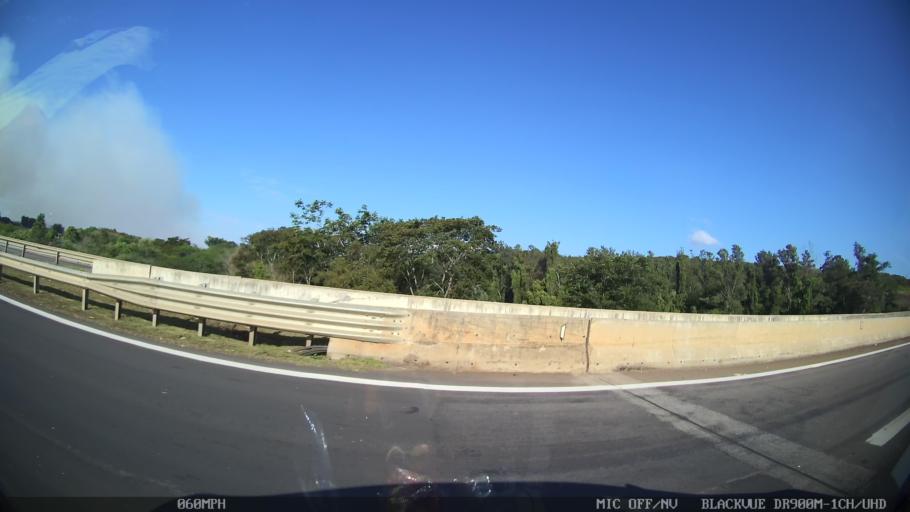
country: BR
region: Sao Paulo
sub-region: Piracicaba
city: Piracicaba
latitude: -22.6999
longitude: -47.6084
